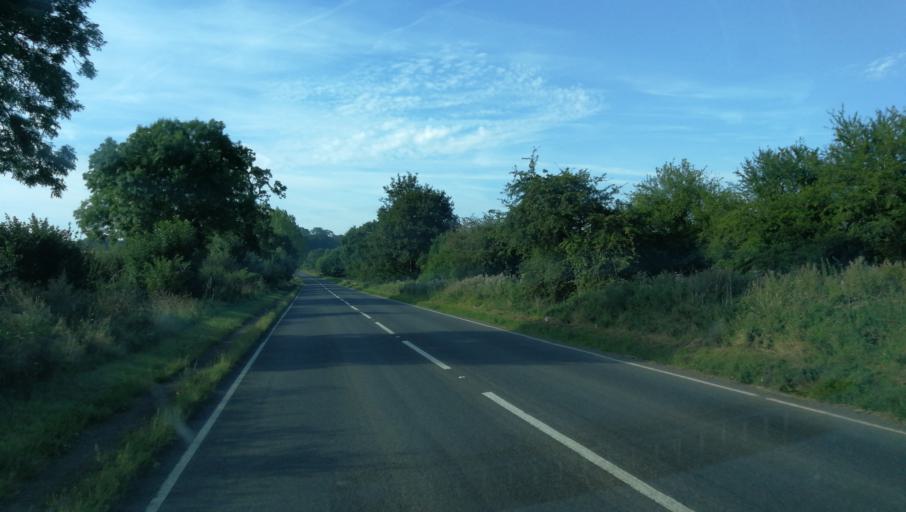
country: GB
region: England
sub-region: Oxfordshire
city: Deddington
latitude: 51.9991
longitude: -1.3215
